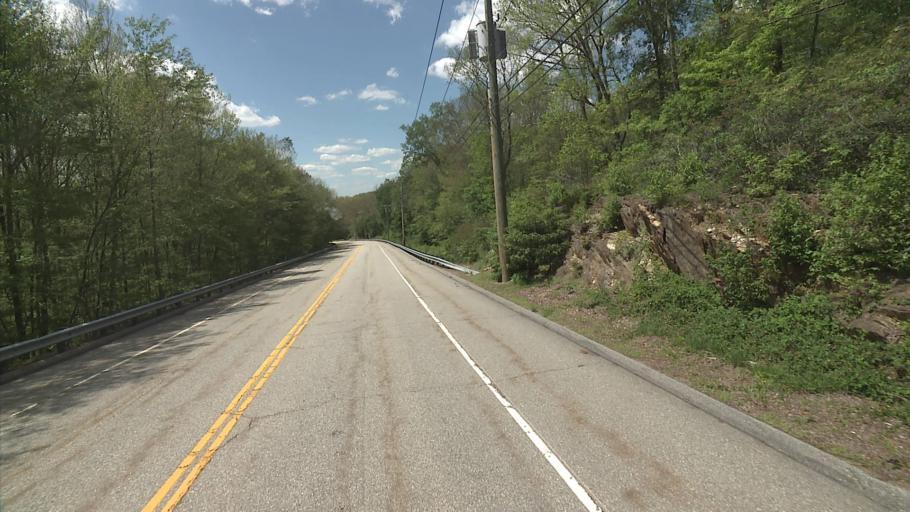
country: US
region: Connecticut
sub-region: Middlesex County
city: Higganum
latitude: 41.5246
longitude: -72.5268
